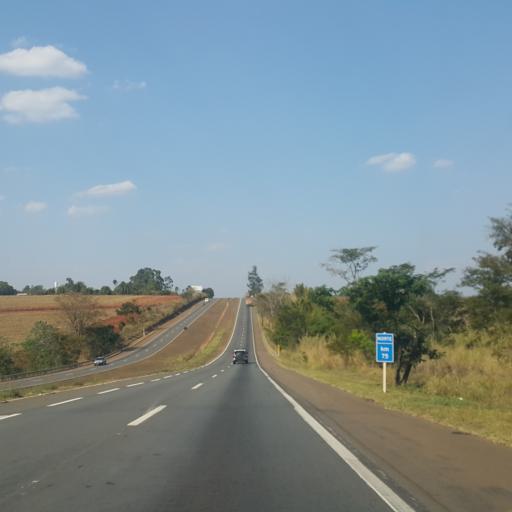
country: BR
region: Goias
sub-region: Abadiania
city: Abadiania
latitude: -16.2775
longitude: -48.7864
